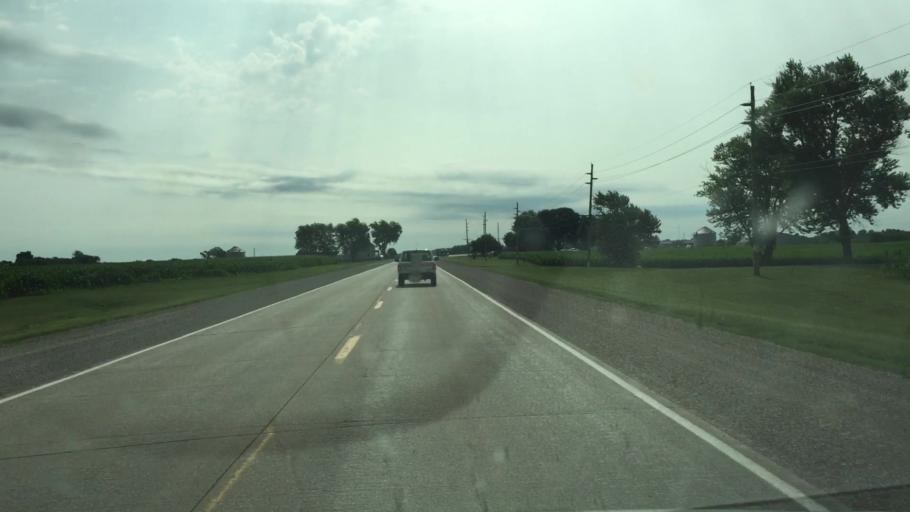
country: US
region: Illinois
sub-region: Hancock County
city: Nauvoo
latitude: 40.6390
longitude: -91.5297
